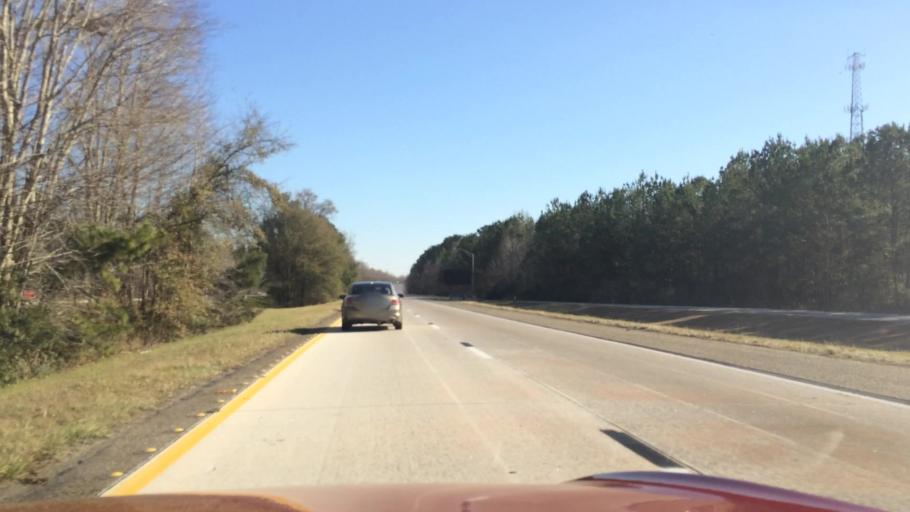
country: US
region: South Carolina
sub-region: Orangeburg County
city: Holly Hill
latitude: 33.2685
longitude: -80.4859
